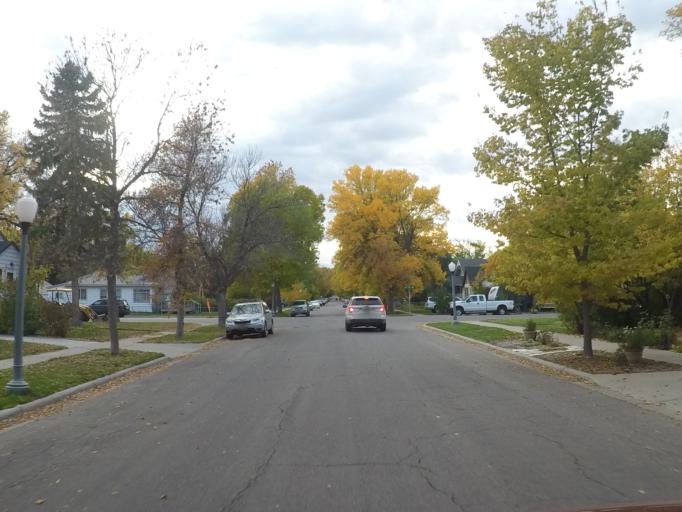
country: US
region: Montana
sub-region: Yellowstone County
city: Billings
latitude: 45.7821
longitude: -108.5249
